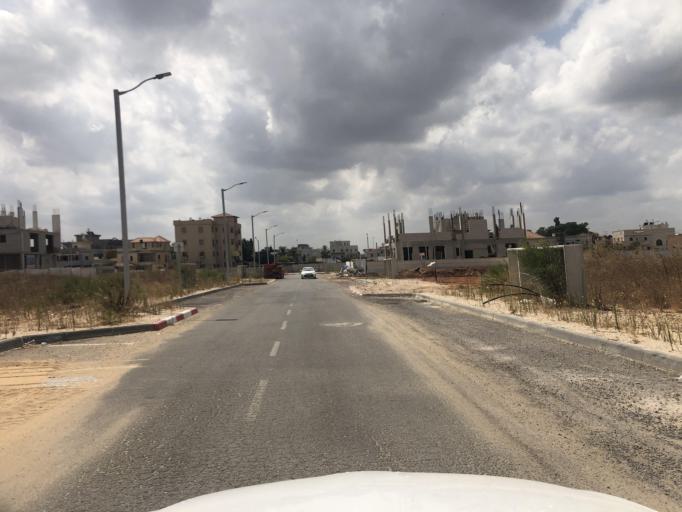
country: IL
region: Central District
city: Jaljulya
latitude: 32.1547
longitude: 34.9591
